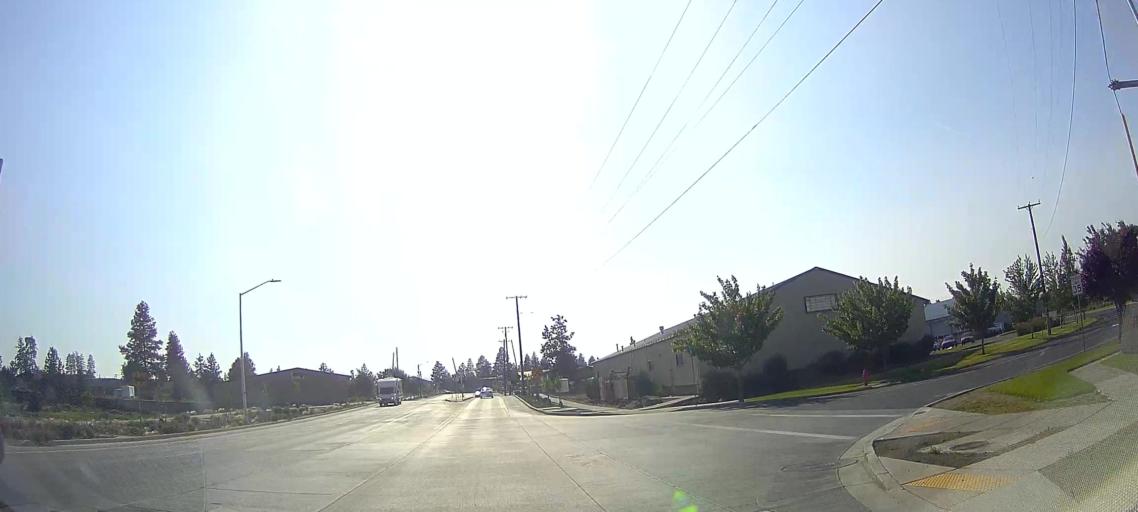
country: US
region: Oregon
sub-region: Deschutes County
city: Bend
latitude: 44.0370
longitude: -121.2878
